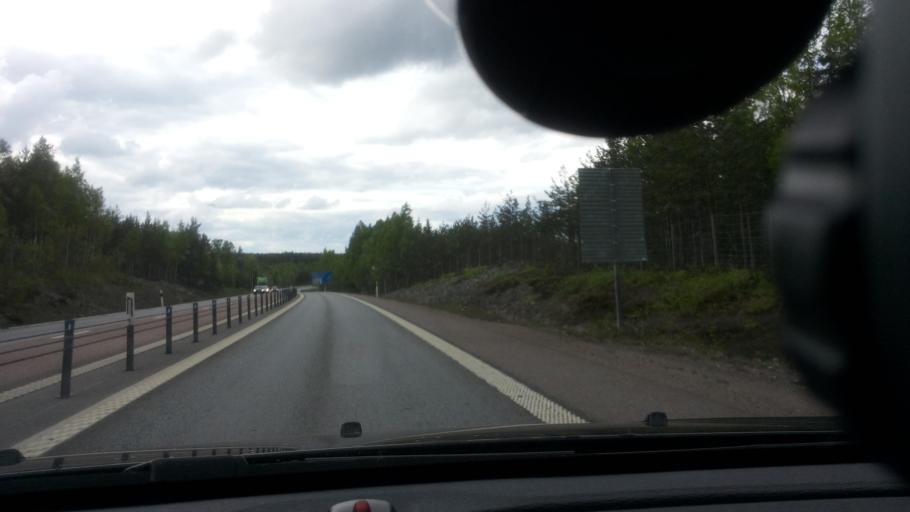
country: SE
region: Gaevleborg
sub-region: Gavle Kommun
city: Norrsundet
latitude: 60.8961
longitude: 17.0282
